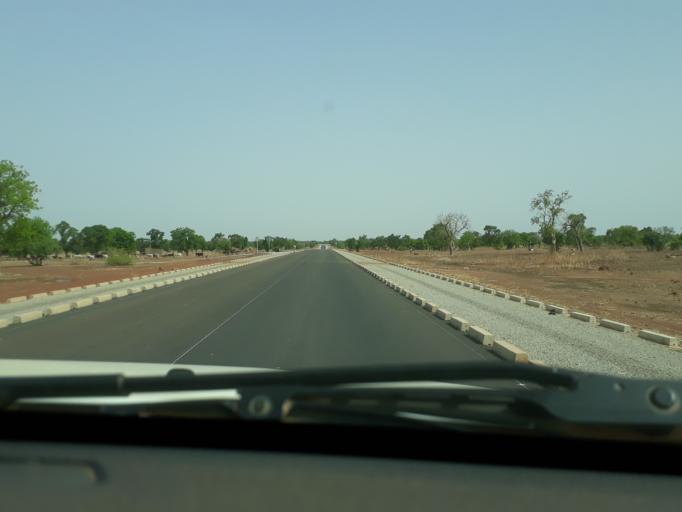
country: BF
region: Plateau-Central
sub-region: Province d'Oubritenga
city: Ziniare
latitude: 12.5636
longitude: -1.4563
